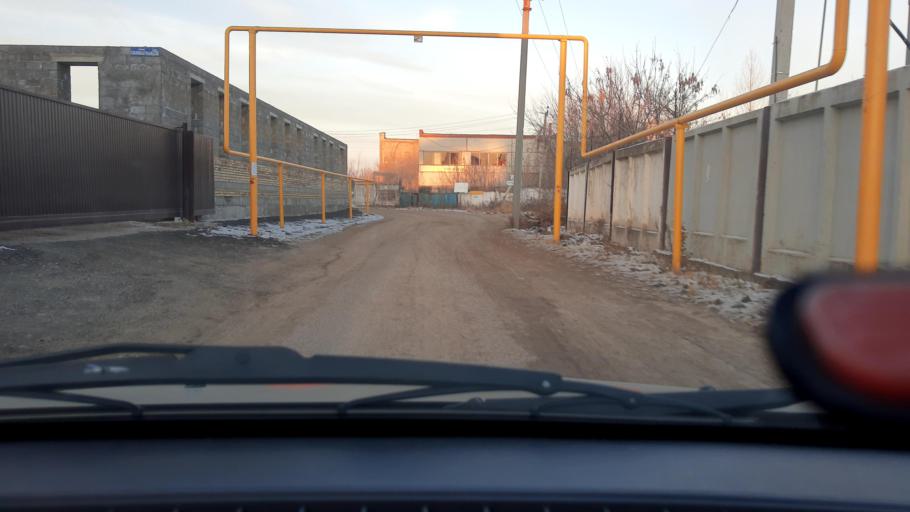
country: RU
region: Bashkortostan
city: Ufa
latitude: 54.7470
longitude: 55.9231
